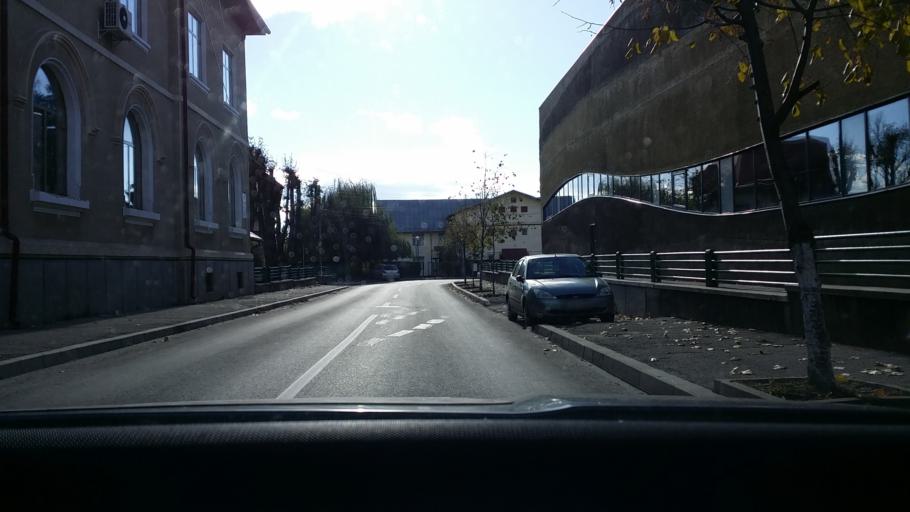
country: RO
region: Prahova
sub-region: Municipiul Campina
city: Campina
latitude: 45.1225
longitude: 25.7316
